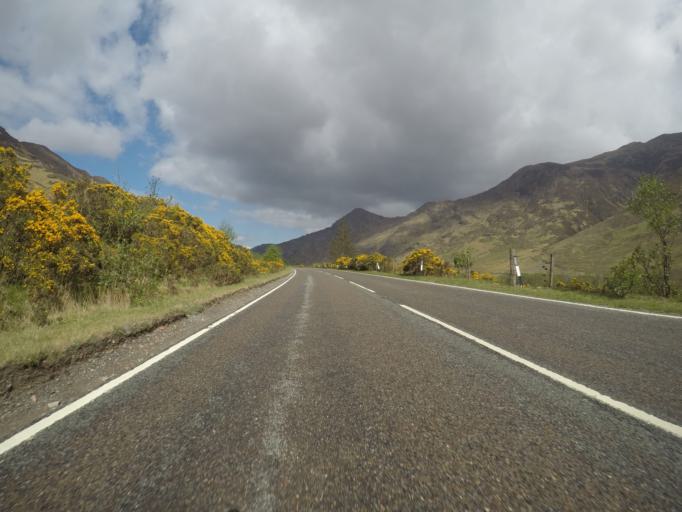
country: GB
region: Scotland
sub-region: Highland
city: Fort William
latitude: 57.1938
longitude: -5.3876
